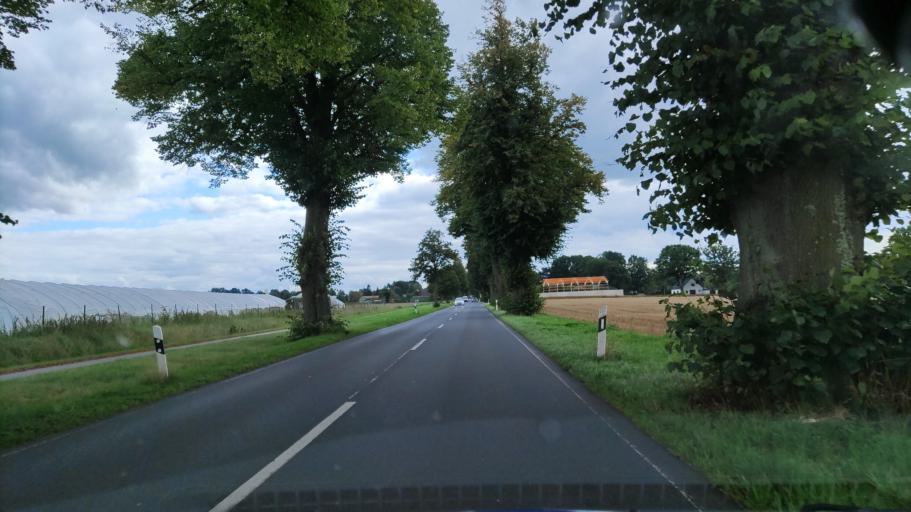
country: DE
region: Lower Saxony
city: Tostedt
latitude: 53.2893
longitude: 9.7123
